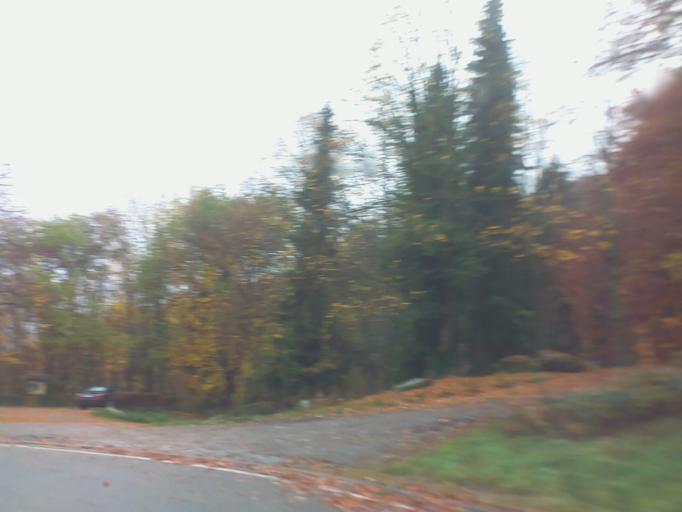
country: DE
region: Hesse
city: Neckarsteinach
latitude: 49.4100
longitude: 8.8429
